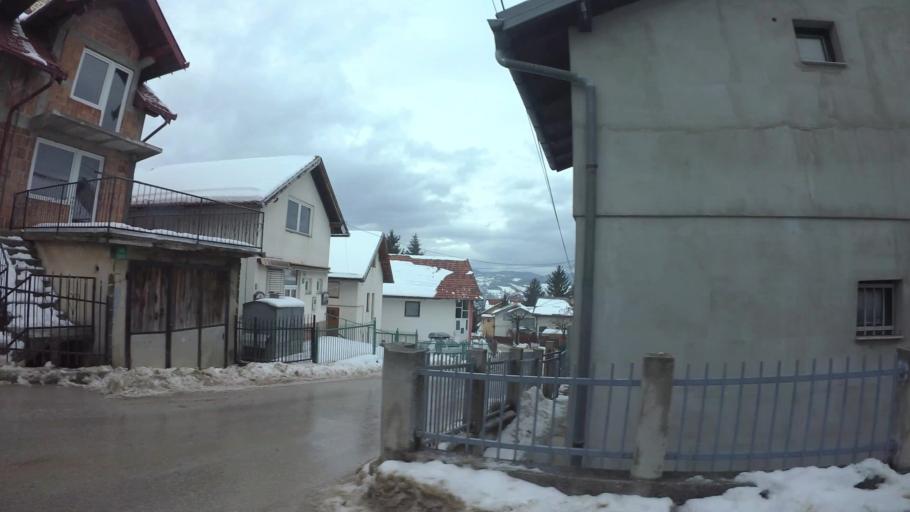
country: BA
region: Federation of Bosnia and Herzegovina
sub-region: Kanton Sarajevo
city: Sarajevo
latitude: 43.8670
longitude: 18.3225
